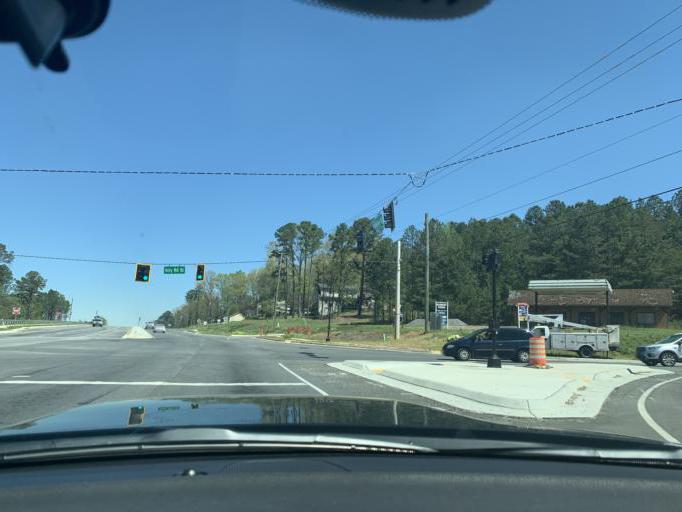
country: US
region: Georgia
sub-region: Forsyth County
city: Cumming
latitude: 34.2004
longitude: -84.1967
